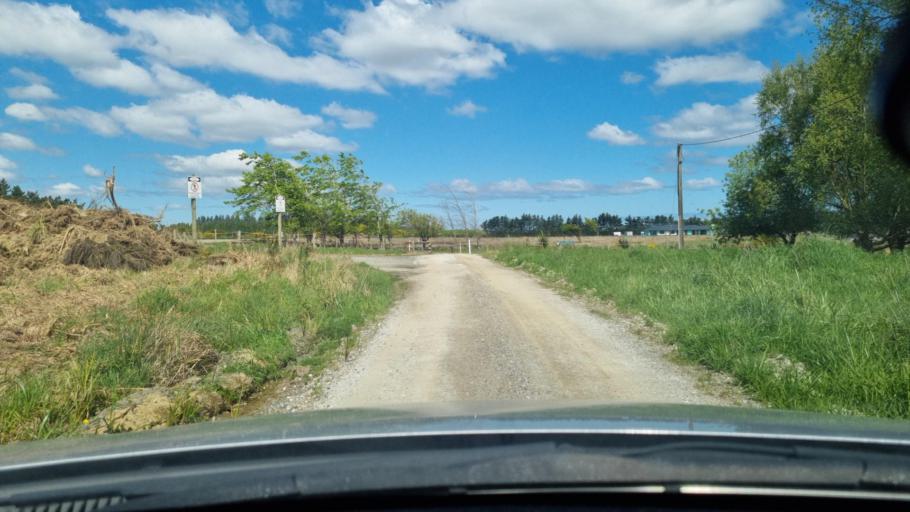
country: NZ
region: Southland
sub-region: Invercargill City
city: Invercargill
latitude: -46.3492
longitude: 168.3400
